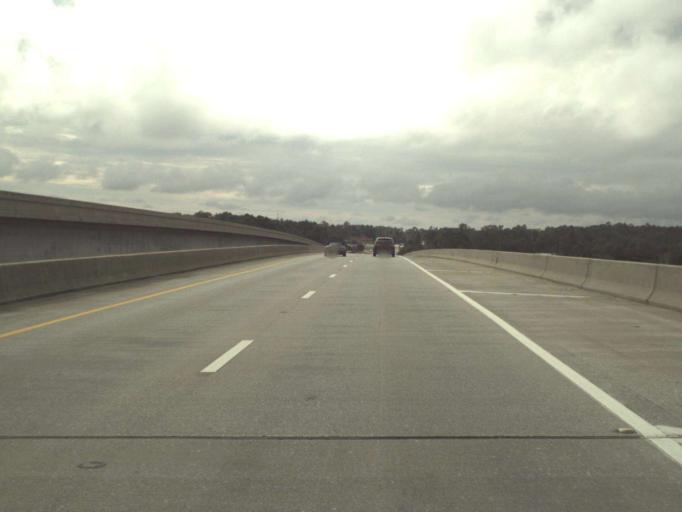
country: US
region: Florida
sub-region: Escambia County
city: Ferry Pass
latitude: 30.5495
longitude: -87.1952
